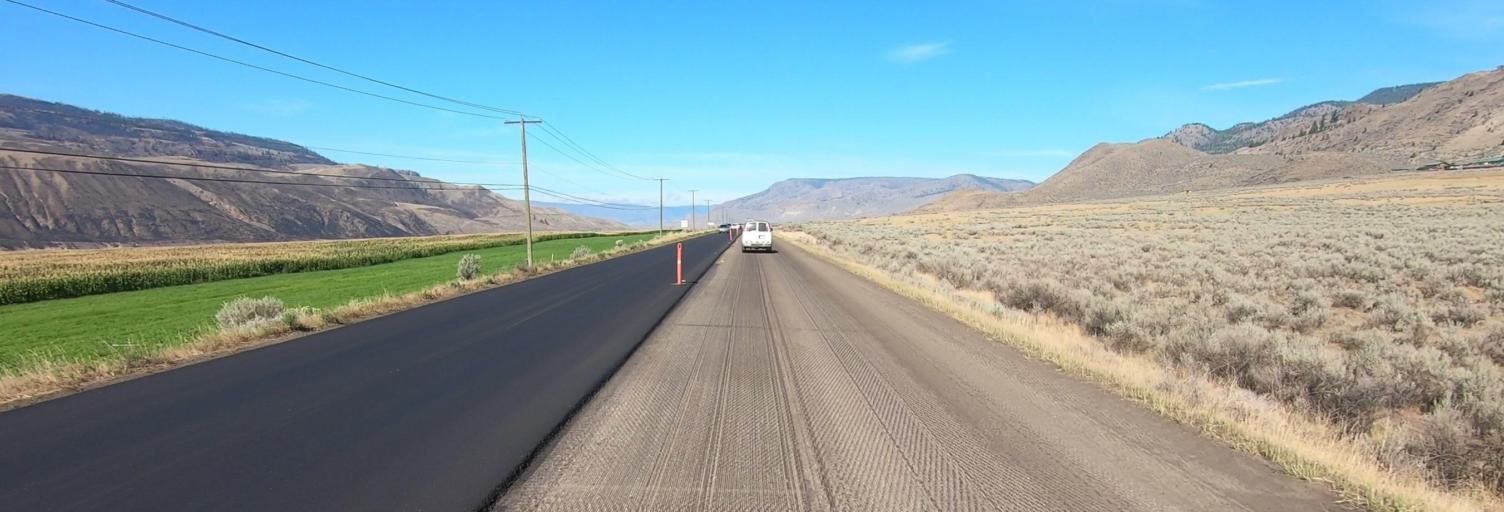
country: CA
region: British Columbia
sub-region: Thompson-Nicola Regional District
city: Ashcroft
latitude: 50.7742
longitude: -121.0392
